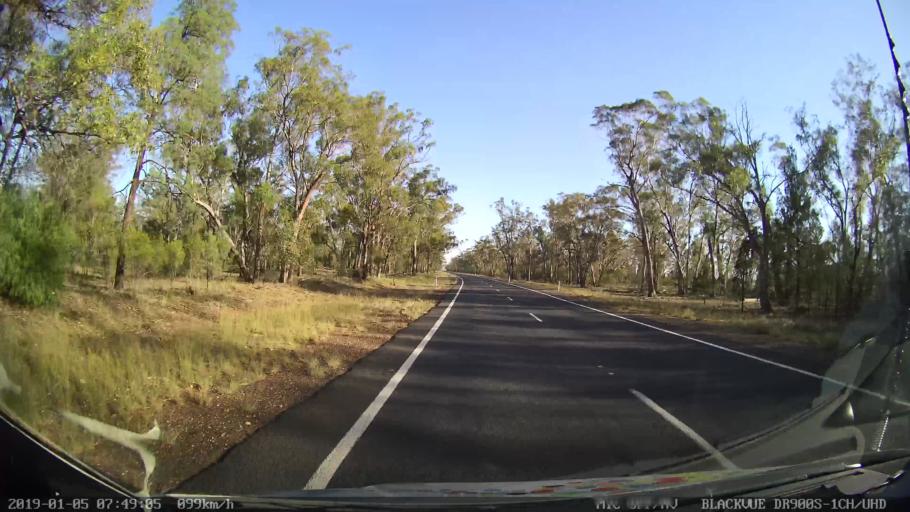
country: AU
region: New South Wales
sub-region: Gilgandra
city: Gilgandra
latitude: -31.8069
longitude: 148.6365
